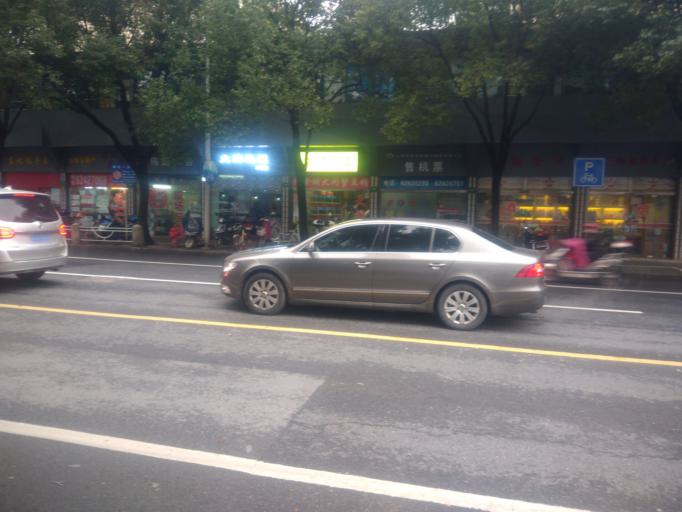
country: CN
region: Shanghai Shi
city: Changzheng
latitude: 31.1917
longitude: 121.3717
